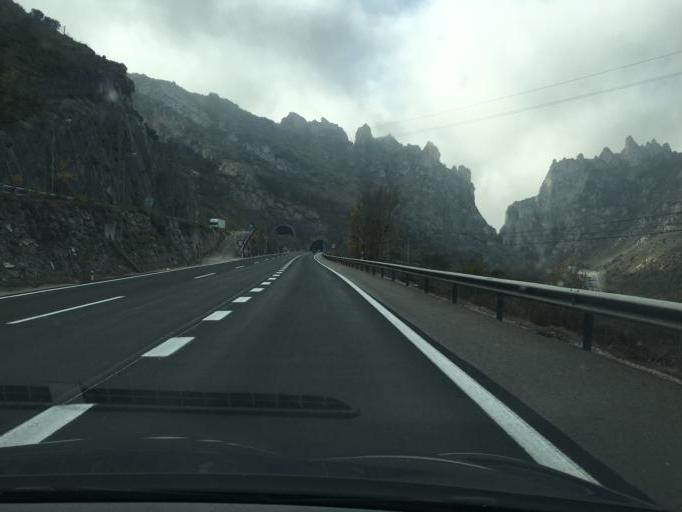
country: ES
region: Castille and Leon
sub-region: Provincia de Burgos
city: Pancorbo
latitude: 42.6437
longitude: -3.0929
